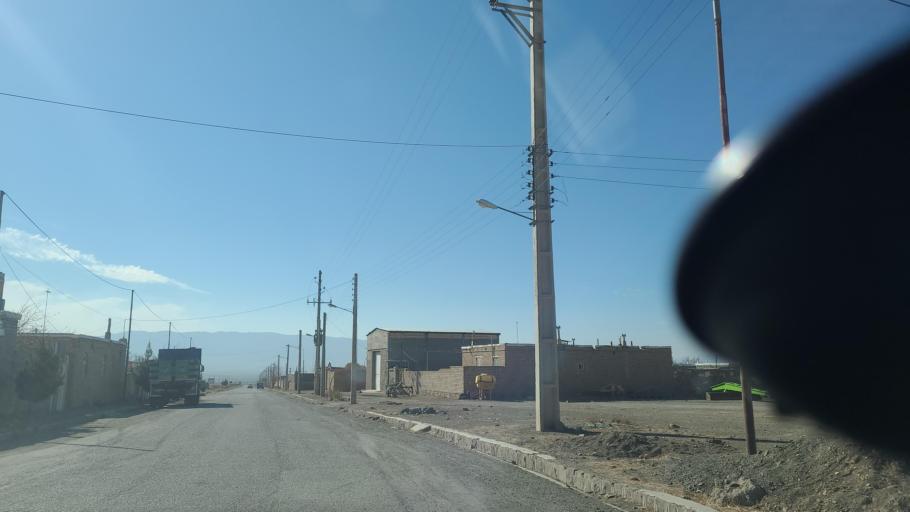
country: IR
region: Razavi Khorasan
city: Dowlatabad
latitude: 35.6205
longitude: 59.4775
